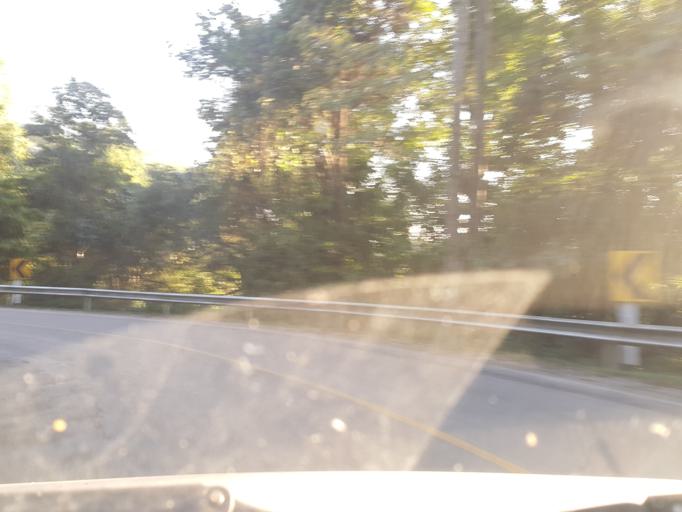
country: TH
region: Mae Hong Son
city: Mae Hi
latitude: 19.2558
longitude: 98.6389
